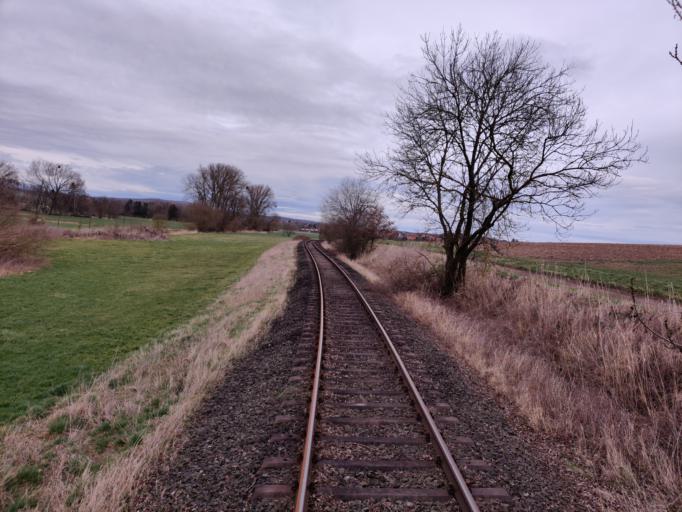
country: DE
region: Lower Saxony
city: Holle
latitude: 52.0741
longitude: 10.1519
